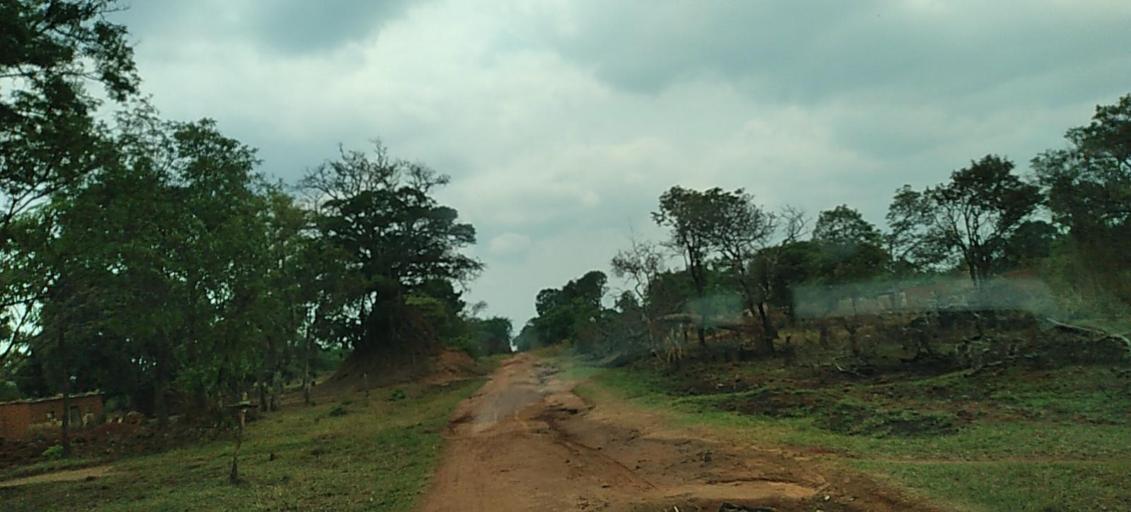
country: ZM
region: North-Western
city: Mwinilunga
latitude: -11.5311
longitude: 24.7849
